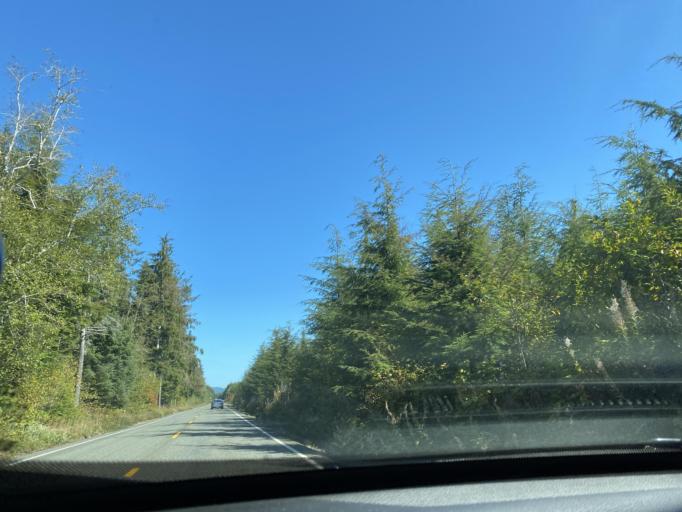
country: US
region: Washington
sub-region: Clallam County
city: Forks
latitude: 47.9243
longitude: -124.4970
